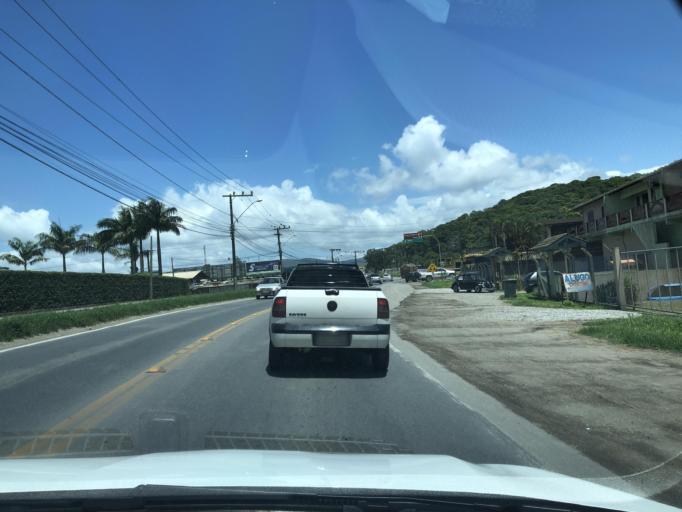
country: BR
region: Santa Catarina
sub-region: Sao Francisco Do Sul
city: Sao Francisco do Sul
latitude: -26.2531
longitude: -48.6160
